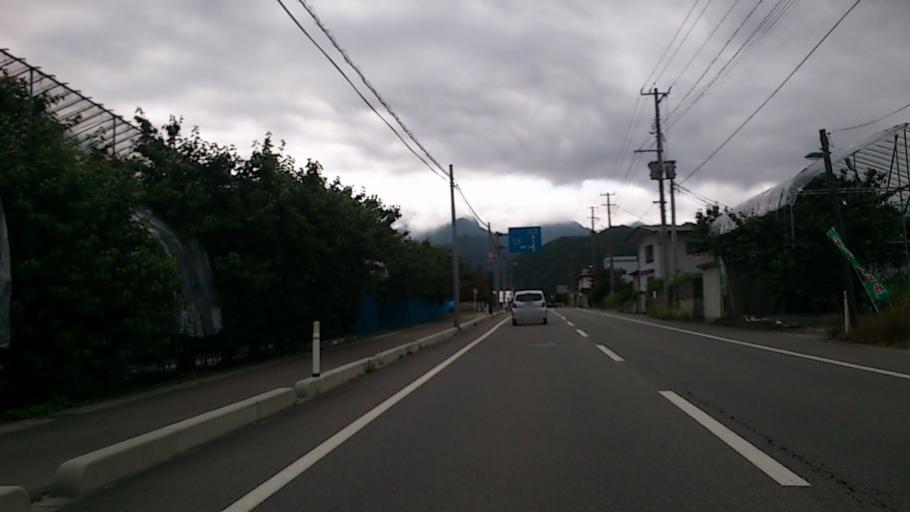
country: JP
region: Yamagata
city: Tendo
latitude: 38.3126
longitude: 140.4144
